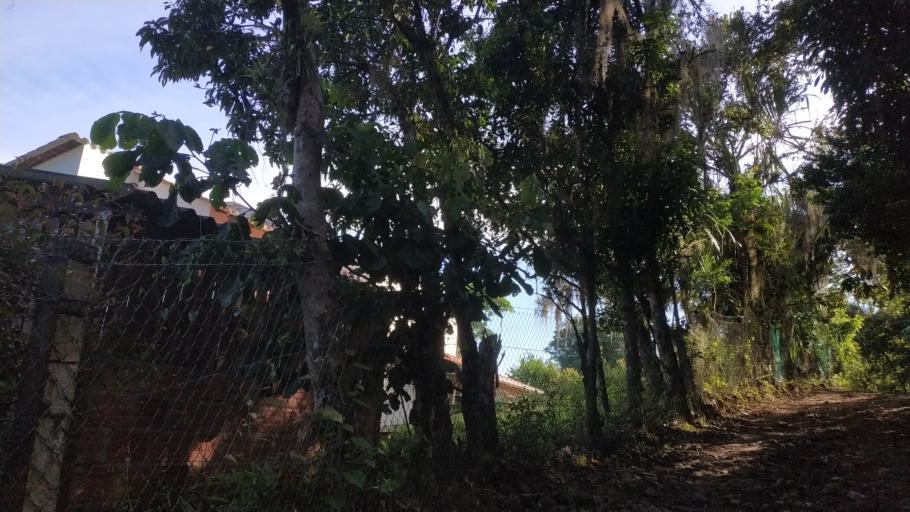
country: CO
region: Santander
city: Guepsa
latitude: 6.0244
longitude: -73.5269
